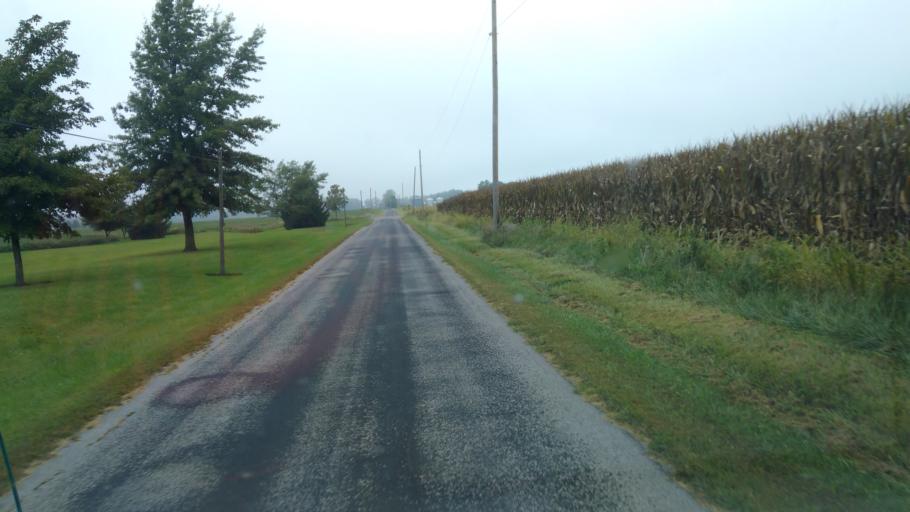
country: US
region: Ohio
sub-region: Hardin County
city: Kenton
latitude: 40.5207
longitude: -83.6007
